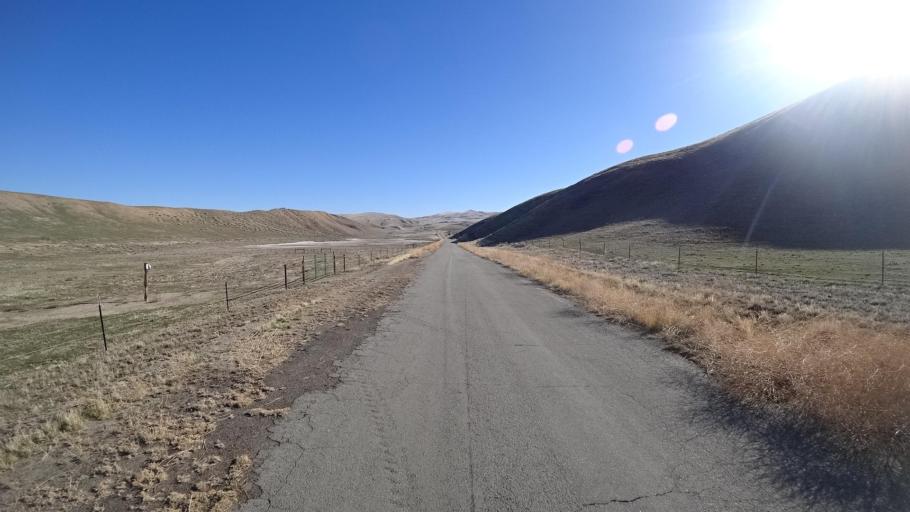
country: US
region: California
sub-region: Kern County
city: Maricopa
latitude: 34.9767
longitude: -119.4630
